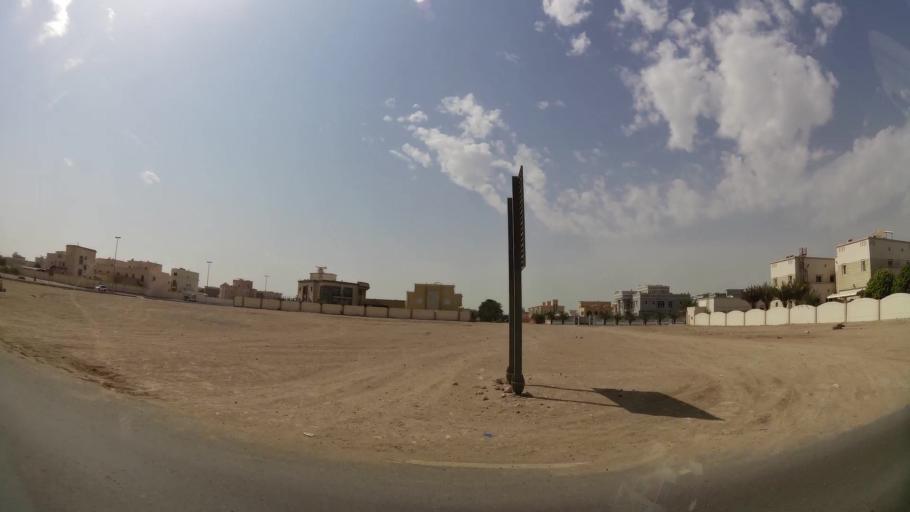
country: AE
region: Abu Dhabi
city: Abu Dhabi
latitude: 24.3425
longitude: 54.5535
